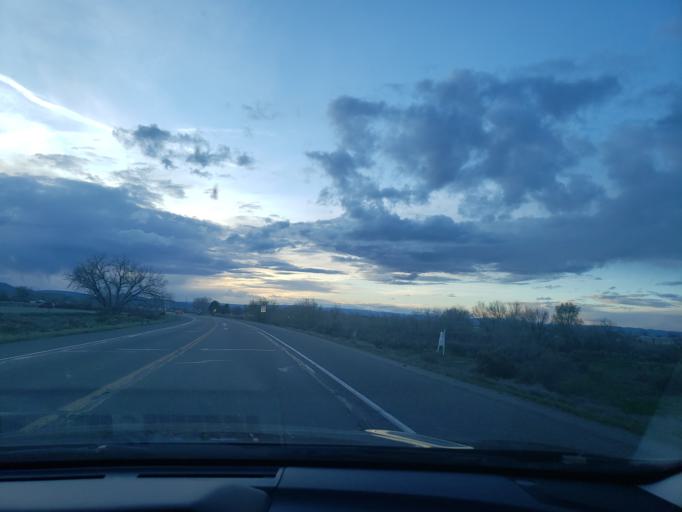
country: US
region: Colorado
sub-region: Mesa County
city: Fruita
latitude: 39.1449
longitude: -108.7114
